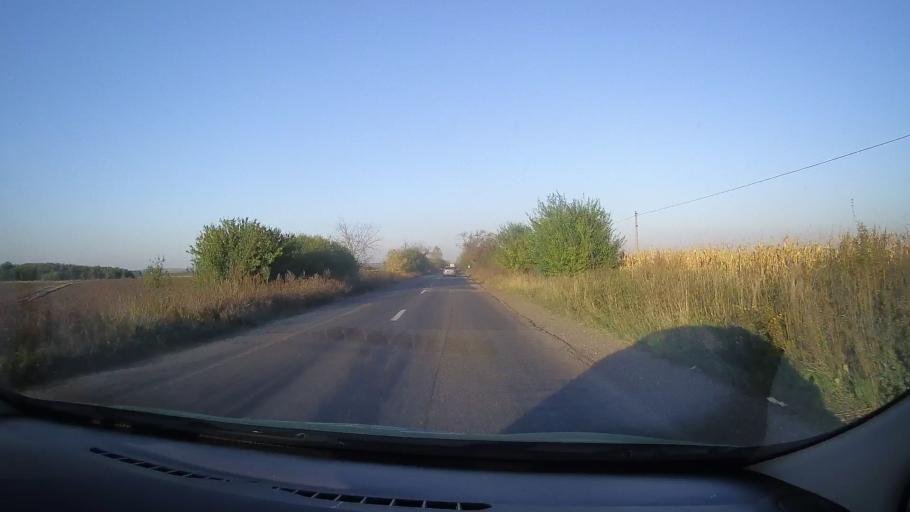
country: RO
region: Bihor
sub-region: Comuna Salard
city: Salard
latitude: 47.1972
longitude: 22.0035
